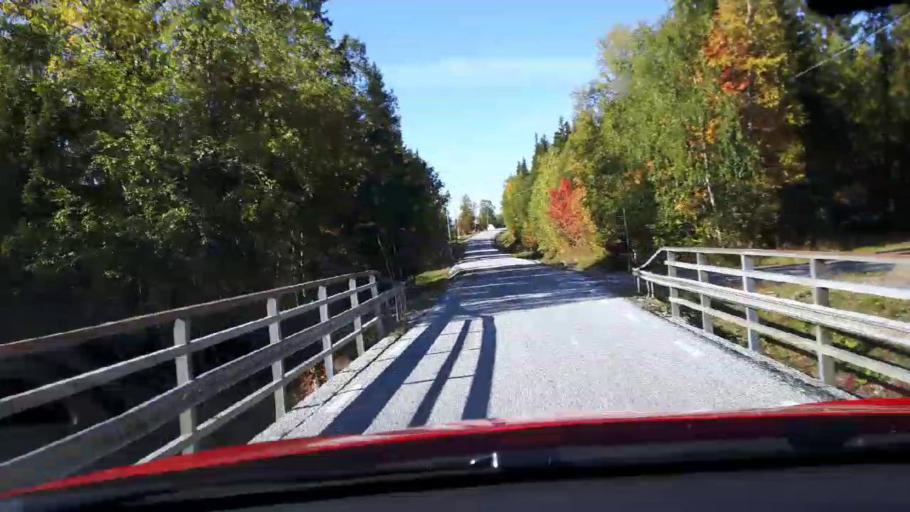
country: NO
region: Nord-Trondelag
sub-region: Royrvik
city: Royrvik
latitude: 64.8279
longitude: 14.1238
